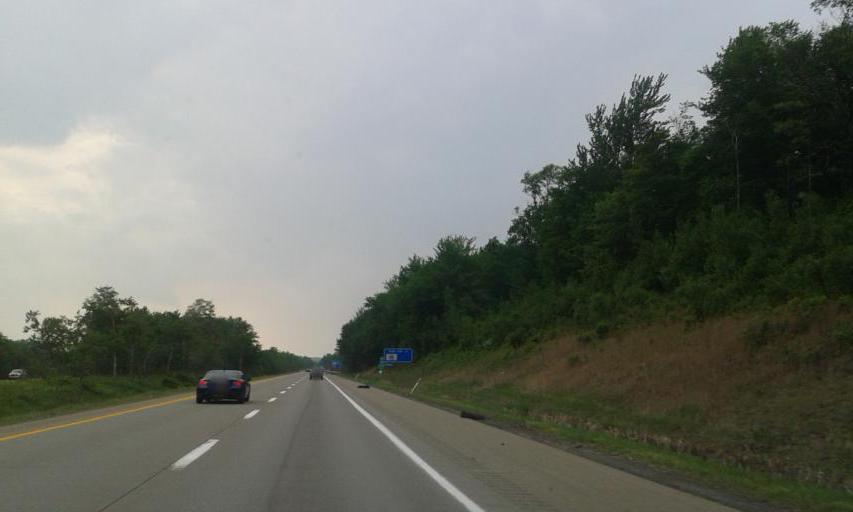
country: US
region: Pennsylvania
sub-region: Monroe County
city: Pocono Pines
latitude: 41.2211
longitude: -75.4821
